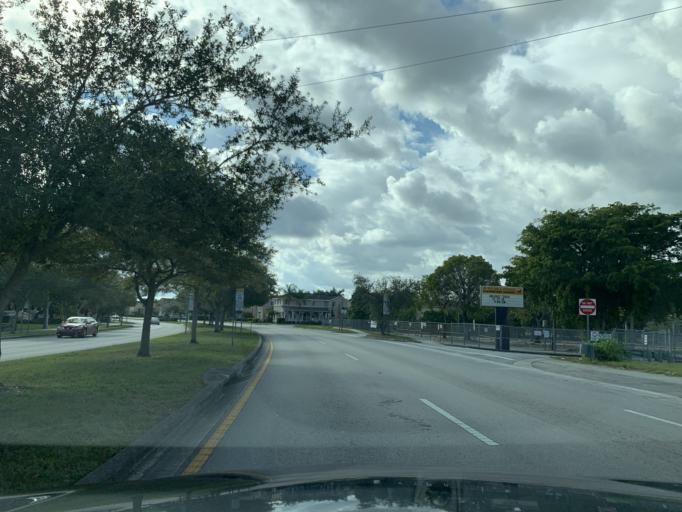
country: US
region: Florida
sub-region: Miami-Dade County
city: Naranja
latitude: 25.5142
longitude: -80.4164
